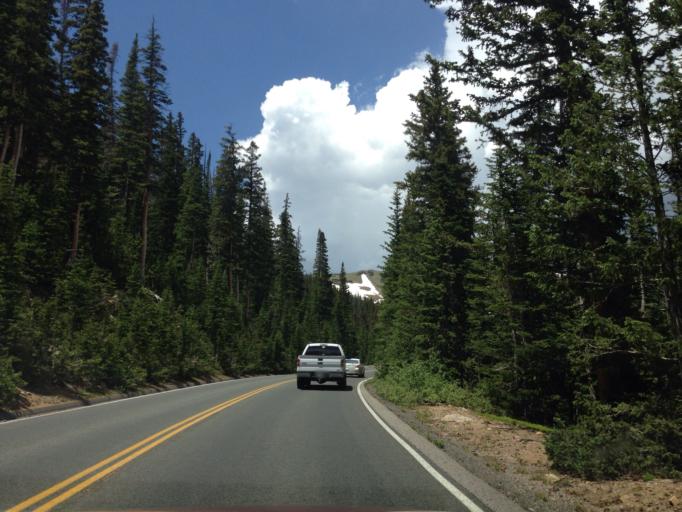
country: US
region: Colorado
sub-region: Larimer County
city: Estes Park
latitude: 40.3854
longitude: -105.6636
